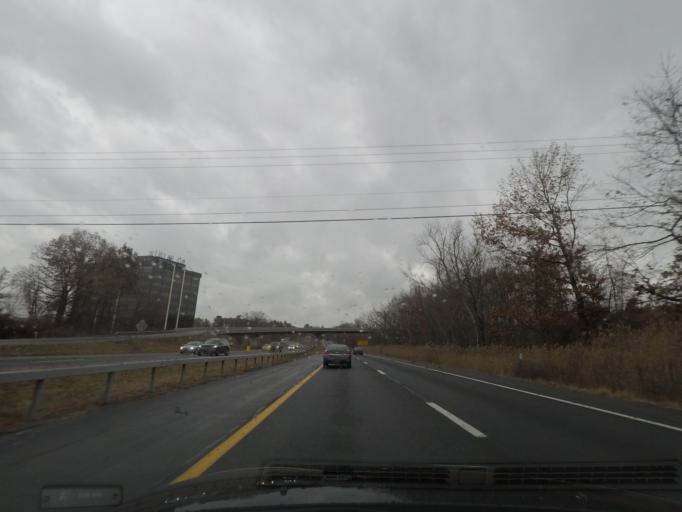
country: US
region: New York
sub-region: Albany County
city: McKownville
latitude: 42.6880
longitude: -73.8431
